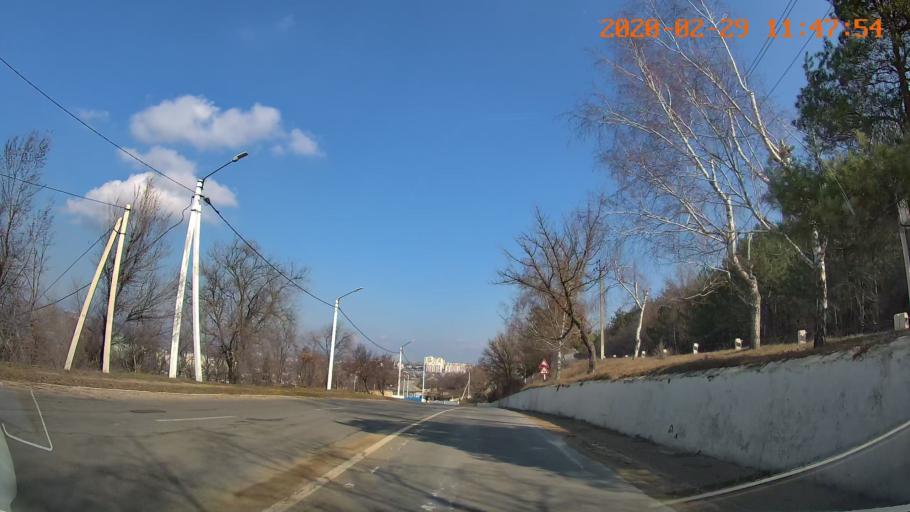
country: MD
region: Rezina
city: Rezina
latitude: 47.7445
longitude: 28.9880
